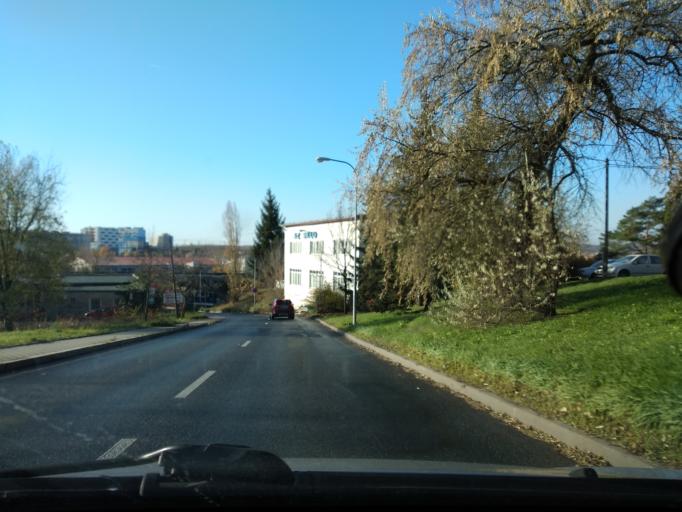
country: CZ
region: South Moravian
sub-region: Mesto Brno
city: Brno
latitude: 49.2240
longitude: 16.6194
